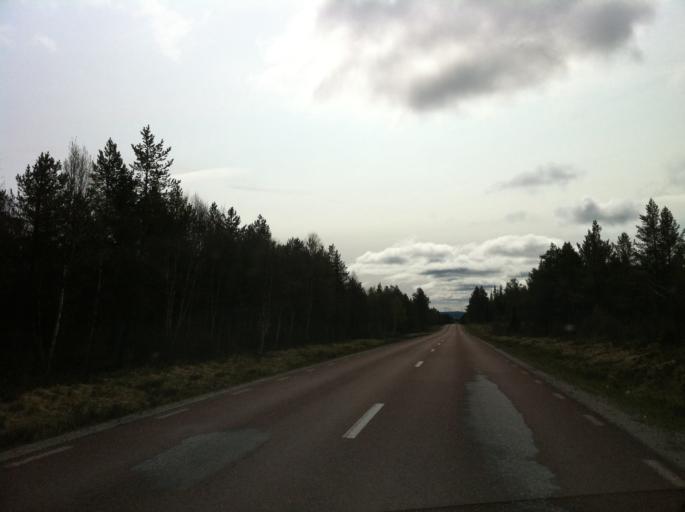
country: NO
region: Hedmark
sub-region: Engerdal
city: Engerdal
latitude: 62.4845
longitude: 12.6559
